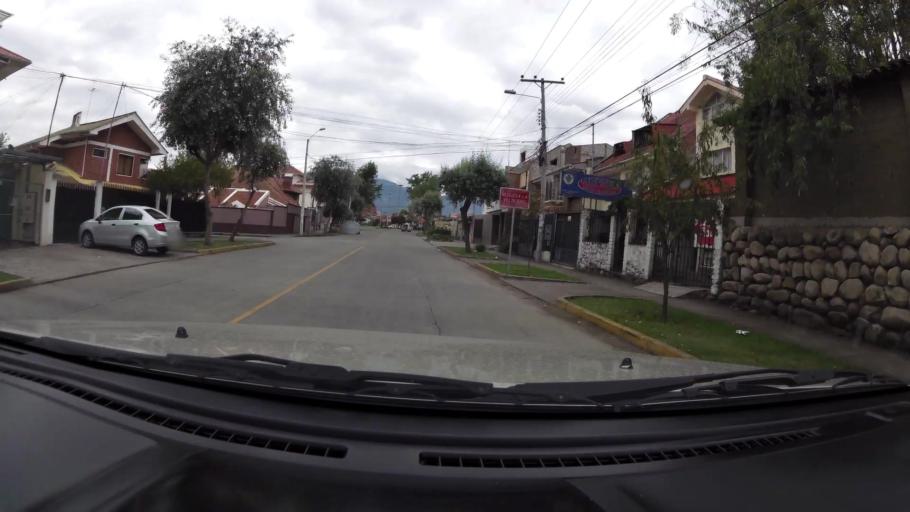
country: EC
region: Azuay
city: Cuenca
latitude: -2.9107
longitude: -79.0183
